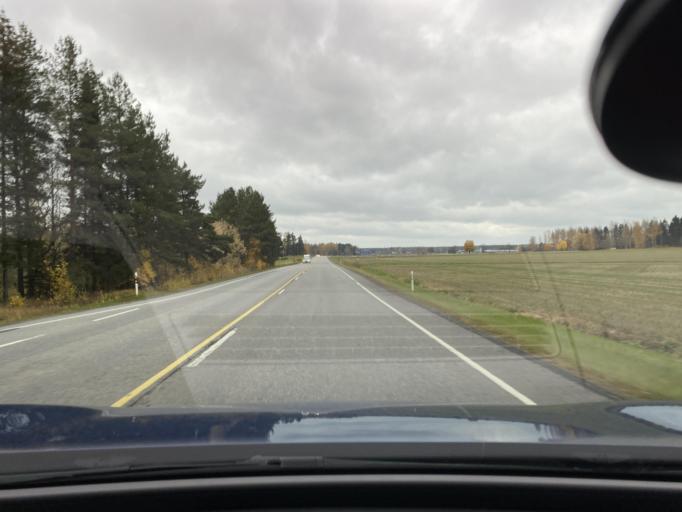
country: FI
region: Satakunta
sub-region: Rauma
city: Kiukainen
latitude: 61.1894
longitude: 22.0604
